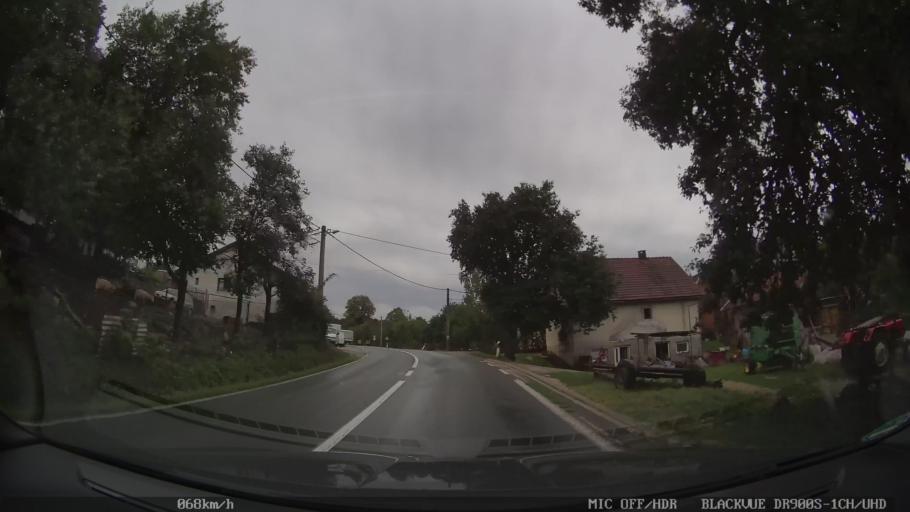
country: HR
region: Licko-Senjska
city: Otocac
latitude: 44.8963
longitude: 15.1830
